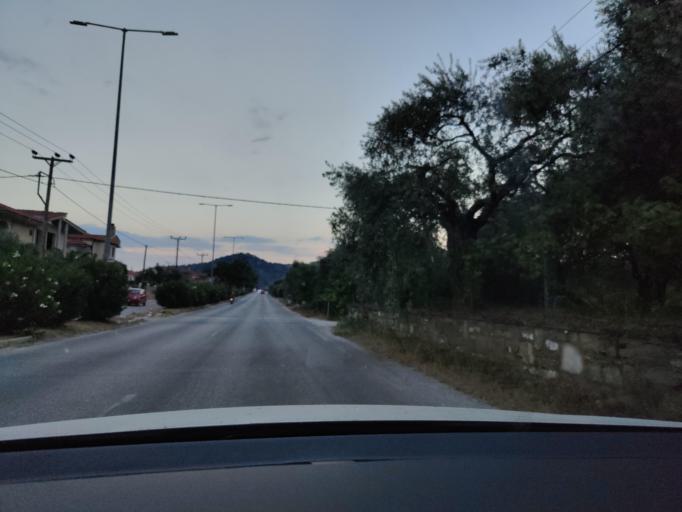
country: GR
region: East Macedonia and Thrace
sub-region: Nomos Kavalas
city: Thasos
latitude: 40.7736
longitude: 24.6951
